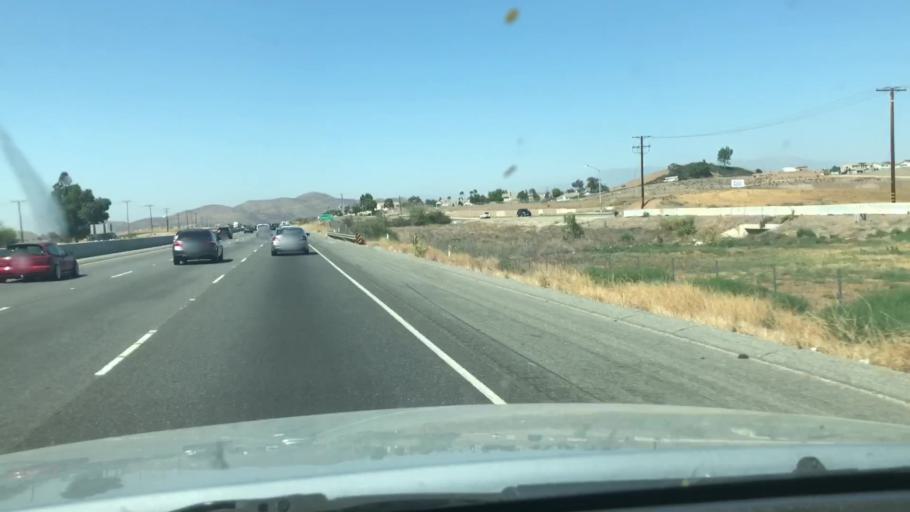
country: US
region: California
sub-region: Riverside County
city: Sun City
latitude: 33.6582
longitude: -117.1708
